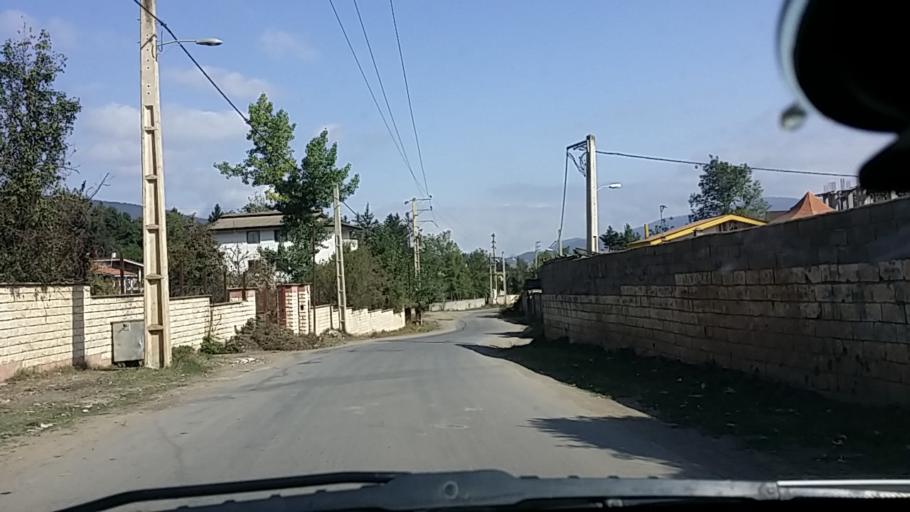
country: IR
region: Mazandaran
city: `Abbasabad
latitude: 36.5042
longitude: 51.1724
